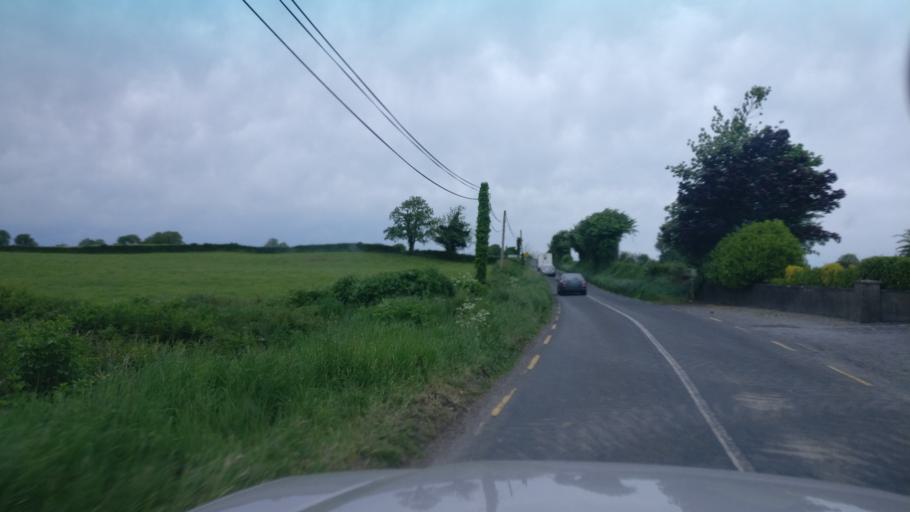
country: IE
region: Connaught
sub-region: County Galway
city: Portumna
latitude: 53.1215
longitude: -8.3211
